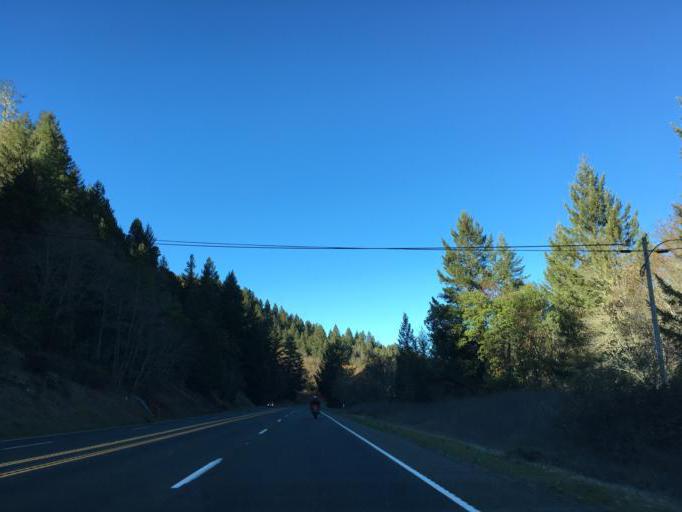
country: US
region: California
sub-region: Mendocino County
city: Laytonville
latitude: 39.5915
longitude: -123.4528
